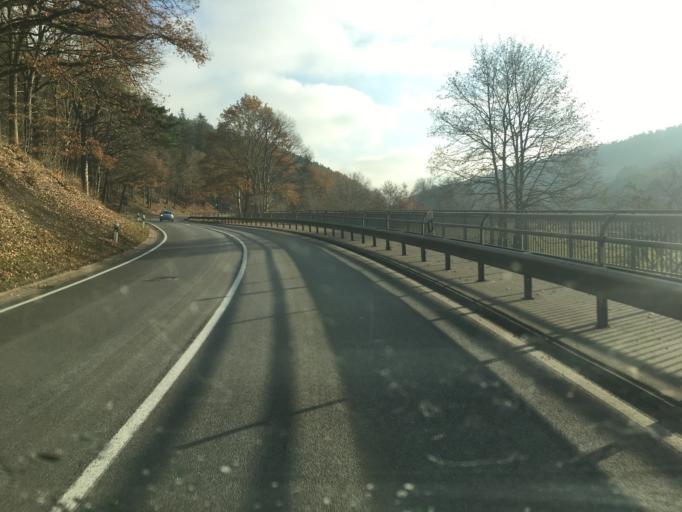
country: DE
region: North Rhine-Westphalia
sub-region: Regierungsbezirk Koln
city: Kall
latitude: 50.5666
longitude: 6.5302
